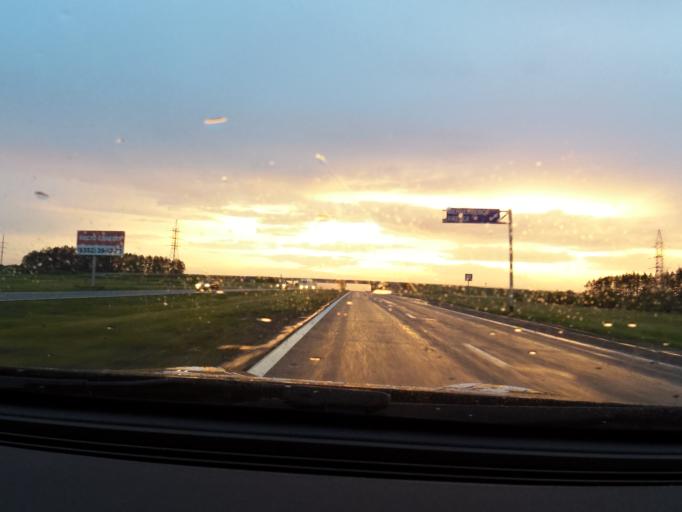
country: RU
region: Tatarstan
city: Yelabuga
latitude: 55.8017
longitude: 52.1440
